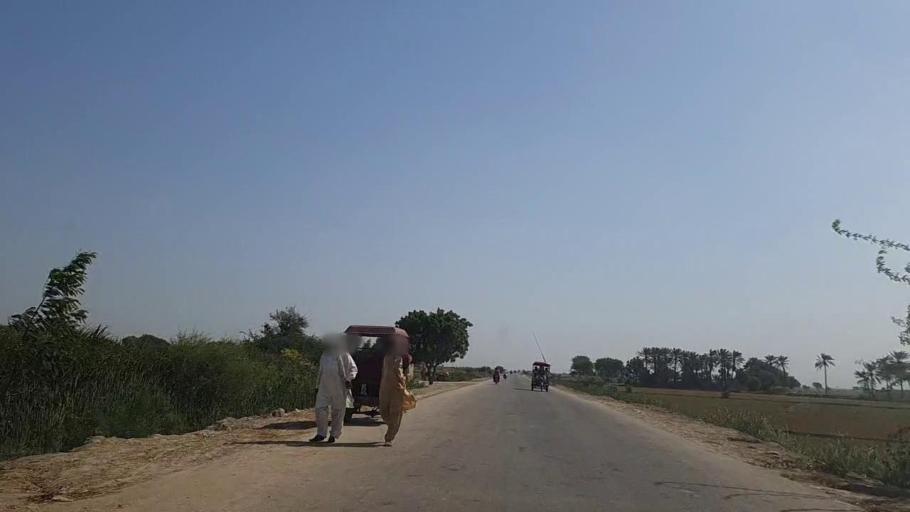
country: PK
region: Sindh
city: Mirpur Batoro
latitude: 24.7590
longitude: 68.2237
